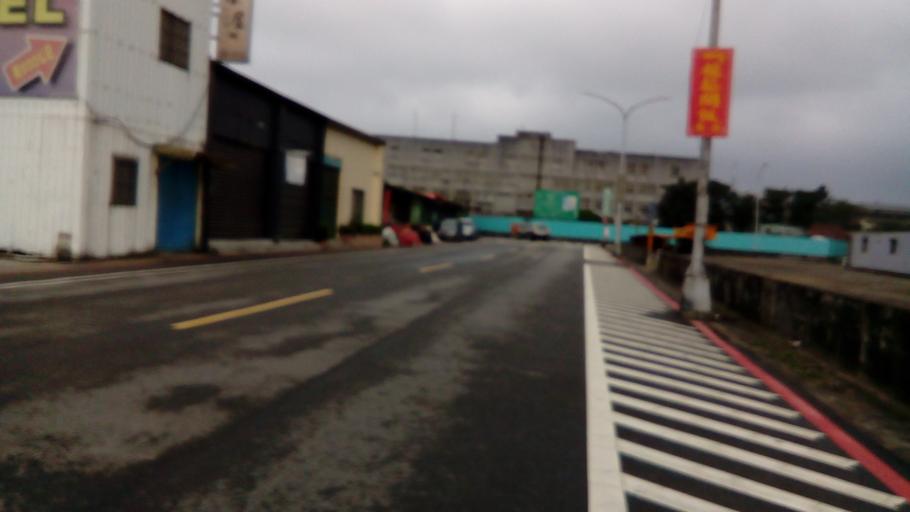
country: TW
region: Taipei
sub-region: Taipei
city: Banqiao
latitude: 25.1811
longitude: 121.4191
